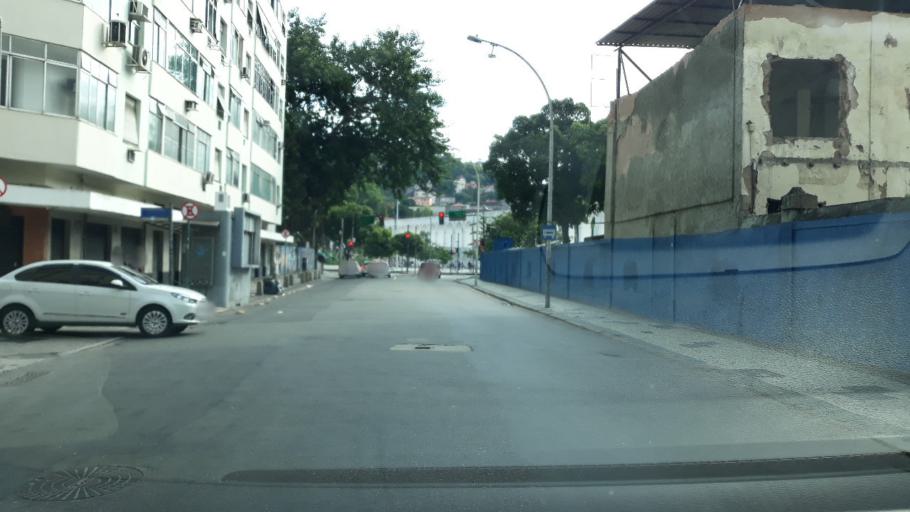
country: BR
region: Rio de Janeiro
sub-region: Rio De Janeiro
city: Rio de Janeiro
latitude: -22.9116
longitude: -43.1785
